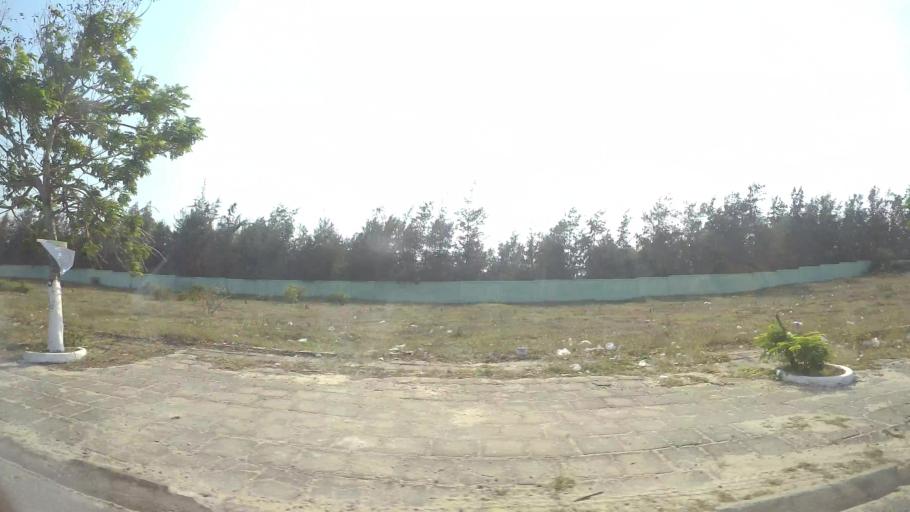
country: VN
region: Da Nang
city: Ngu Hanh Son
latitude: 15.9592
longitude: 108.2903
